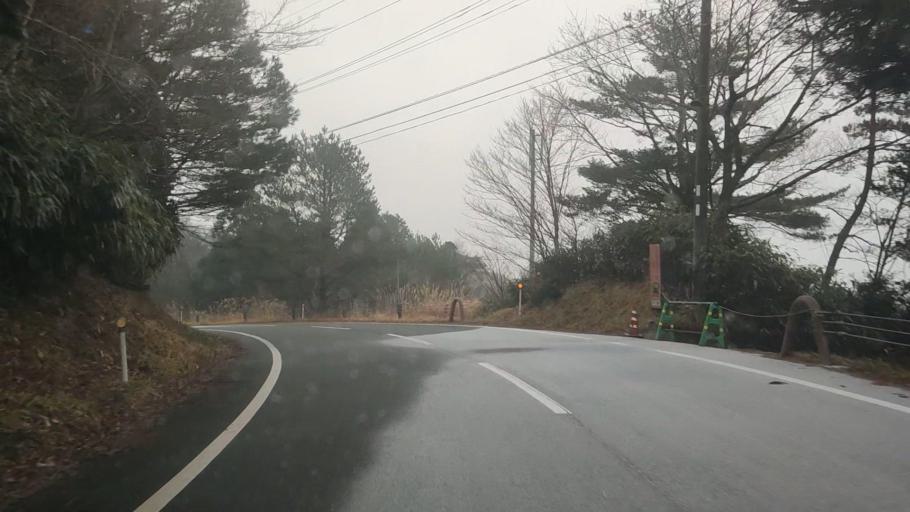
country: JP
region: Kumamoto
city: Matsubase
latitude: 32.5739
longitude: 130.9033
